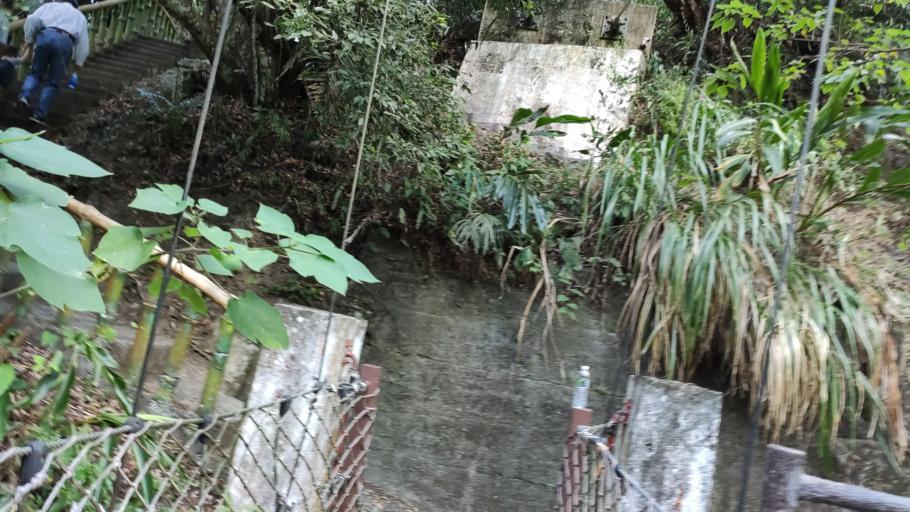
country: TW
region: Taiwan
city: Daxi
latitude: 24.7896
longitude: 121.3748
